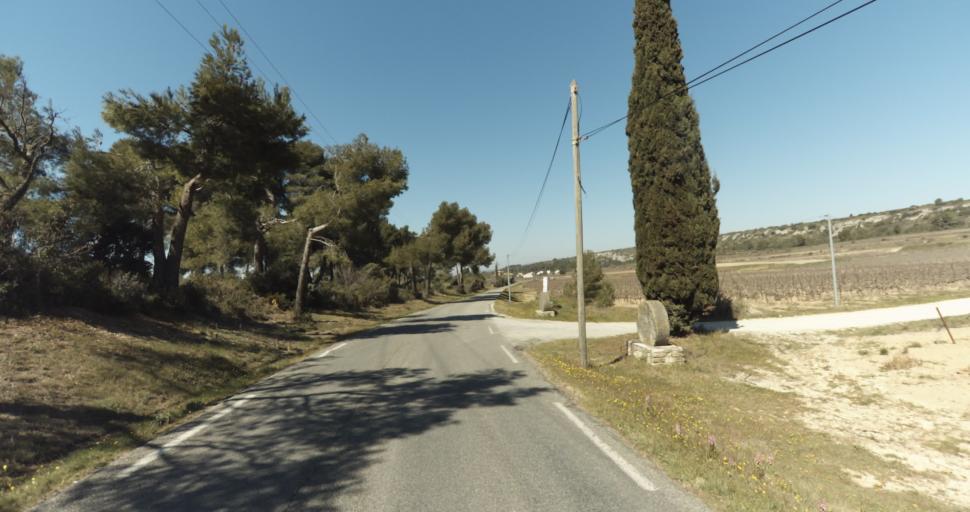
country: FR
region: Provence-Alpes-Cote d'Azur
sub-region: Departement des Bouches-du-Rhone
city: La Fare-les-Oliviers
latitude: 43.6024
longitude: 5.1925
